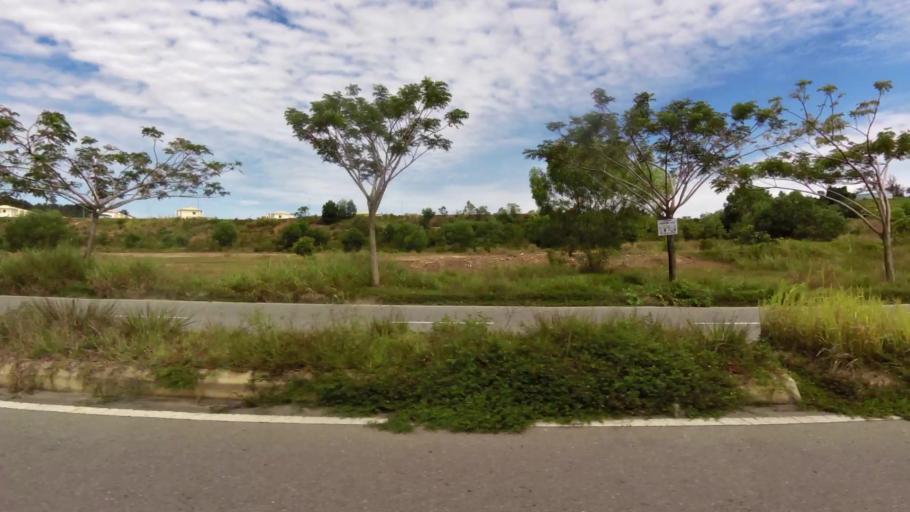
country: BN
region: Brunei and Muara
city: Bandar Seri Begawan
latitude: 4.9864
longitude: 115.0160
